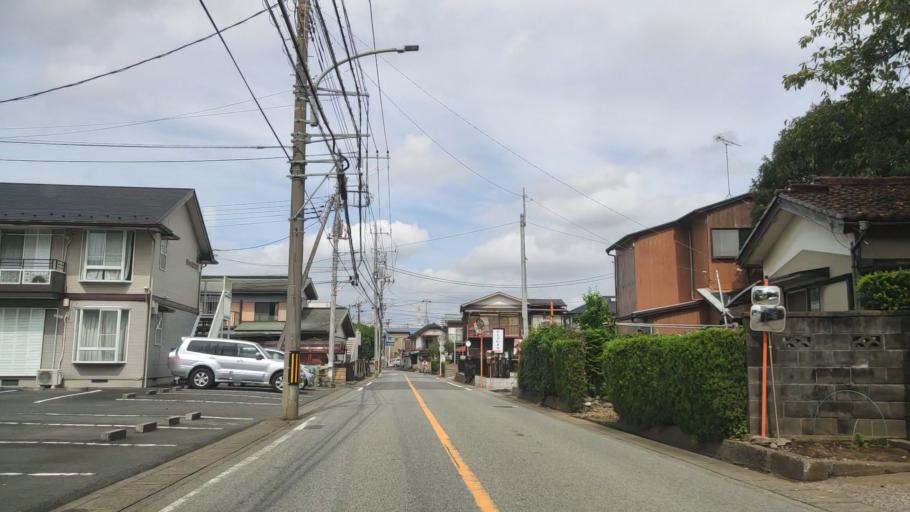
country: JP
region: Kanagawa
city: Minami-rinkan
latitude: 35.4885
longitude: 139.4730
